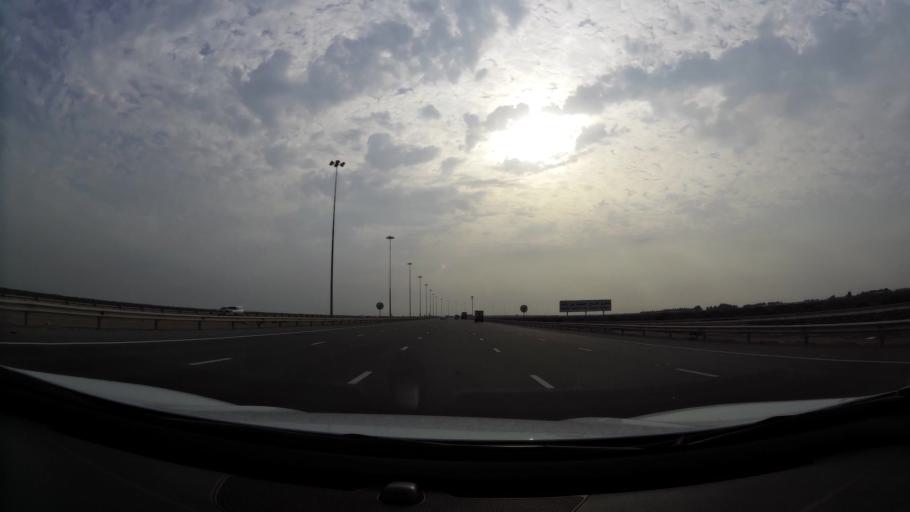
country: AE
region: Abu Dhabi
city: Abu Dhabi
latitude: 24.5474
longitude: 54.4681
